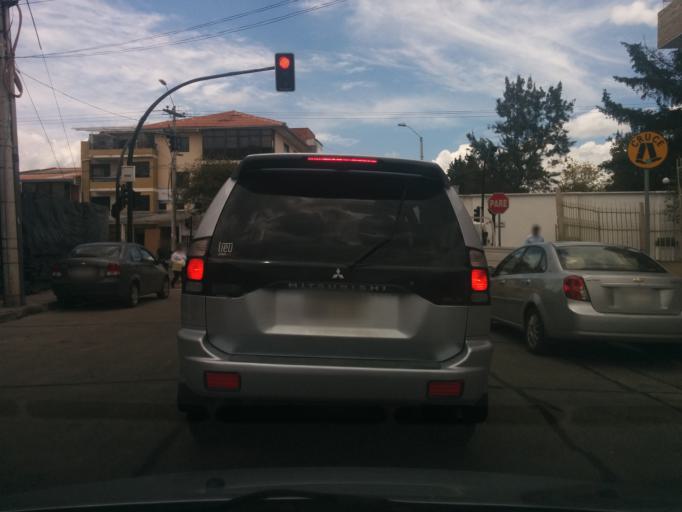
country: EC
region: Azuay
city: Cuenca
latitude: -2.8989
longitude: -78.9926
